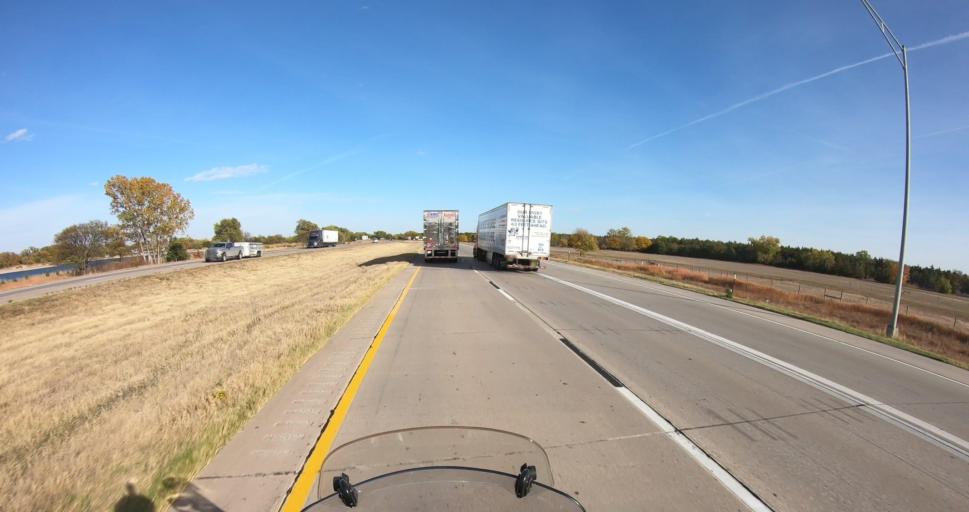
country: US
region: Nebraska
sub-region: Buffalo County
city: Kearney
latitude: 40.6701
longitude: -99.0222
